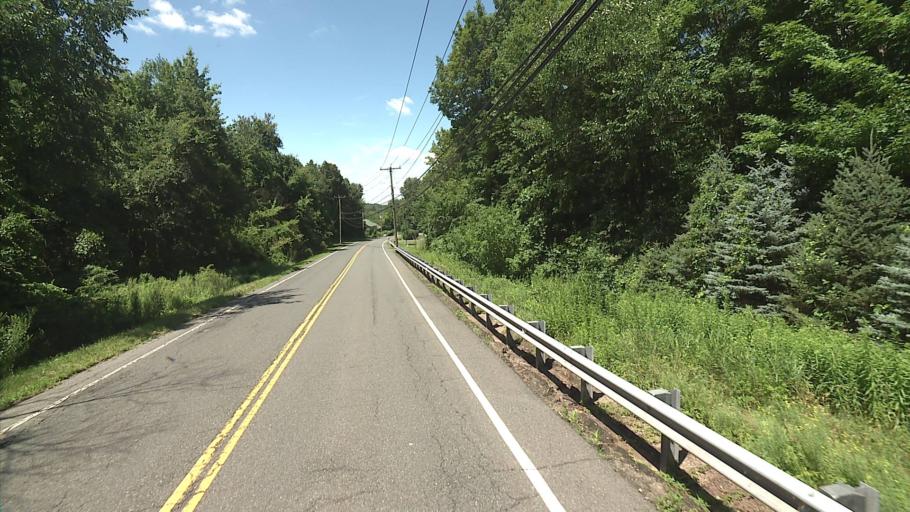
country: US
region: Massachusetts
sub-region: Hampden County
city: Southwick
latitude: 42.0139
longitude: -72.7267
